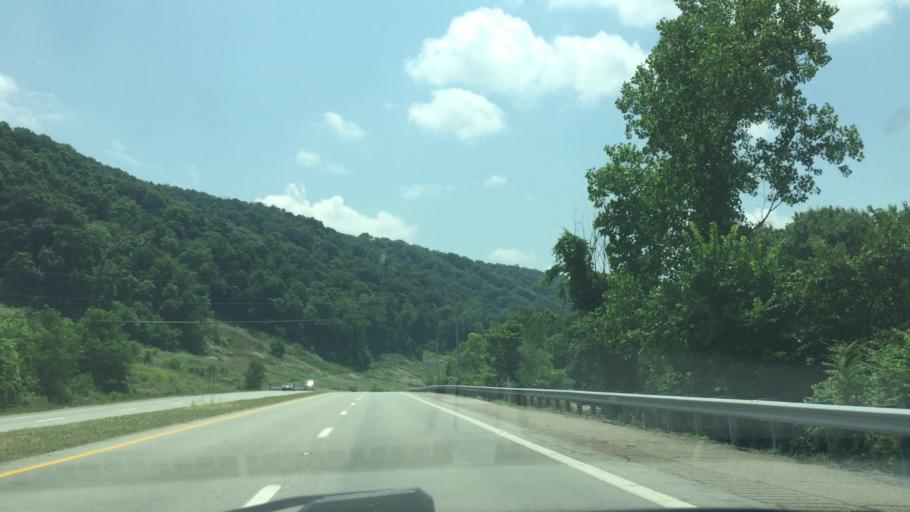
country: US
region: Ohio
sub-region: Belmont County
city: Powhatan Point
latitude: 39.8816
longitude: -80.7860
